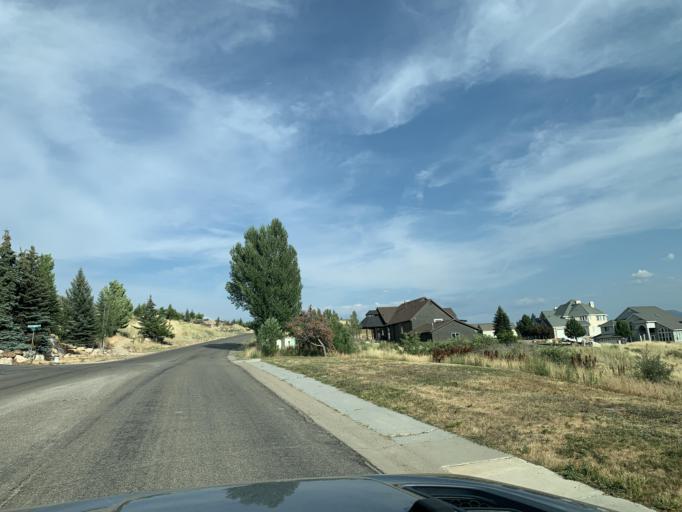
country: US
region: Utah
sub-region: Weber County
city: Wolf Creek
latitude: 41.3298
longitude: -111.8225
